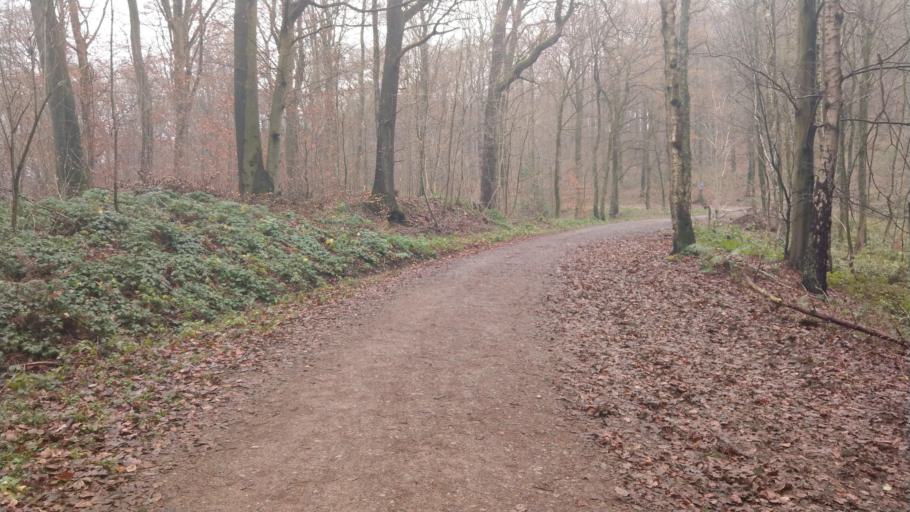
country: BE
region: Wallonia
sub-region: Province de Liege
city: La Calamine
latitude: 50.7325
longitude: 6.0576
